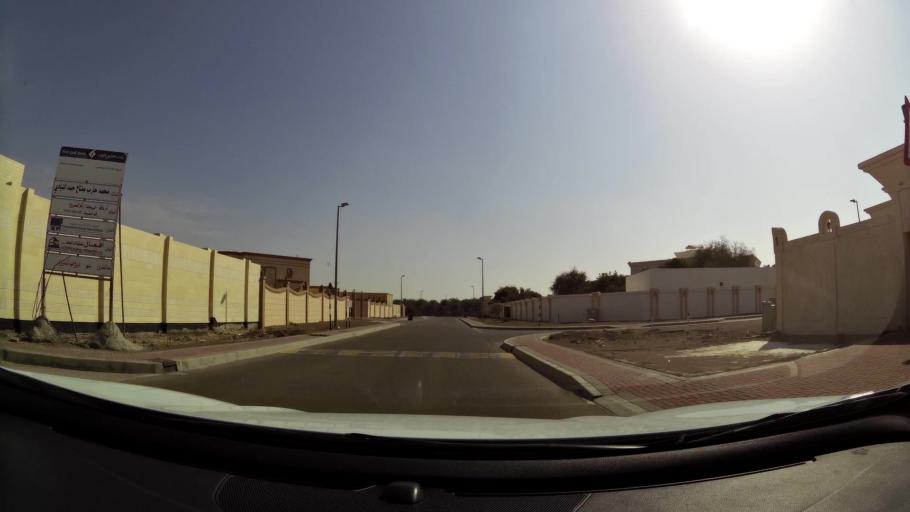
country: AE
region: Abu Dhabi
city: Al Ain
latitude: 24.0880
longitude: 55.9329
